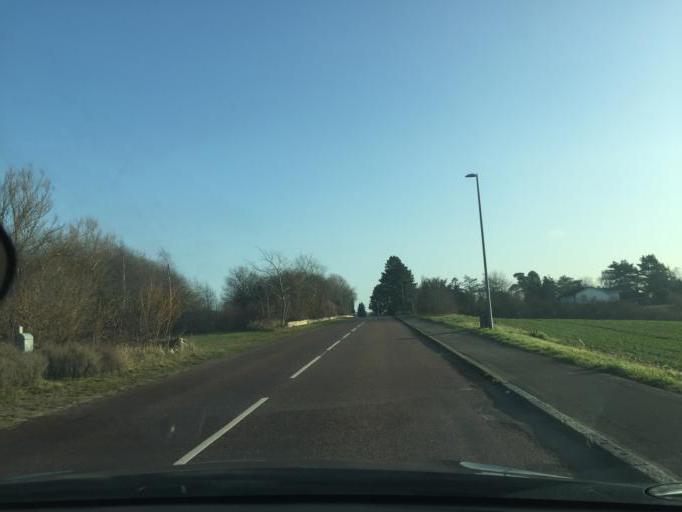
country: DK
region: South Denmark
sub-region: Faaborg-Midtfyn Kommune
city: Faaborg
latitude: 55.1276
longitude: 10.2245
